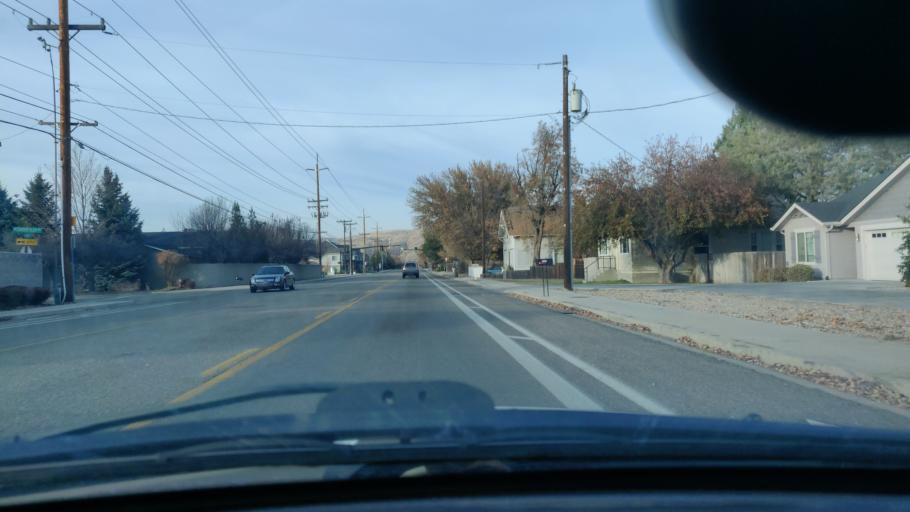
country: US
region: Idaho
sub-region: Ada County
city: Garden City
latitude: 43.6700
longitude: -116.2792
